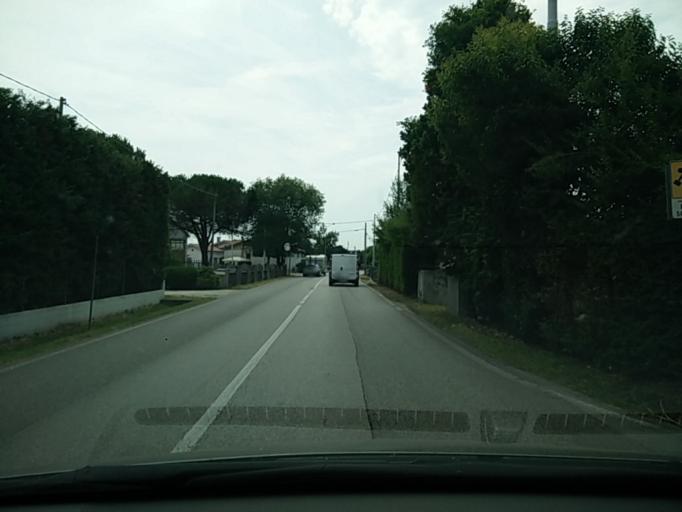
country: IT
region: Veneto
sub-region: Provincia di Treviso
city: Varago
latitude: 45.7334
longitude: 12.2891
